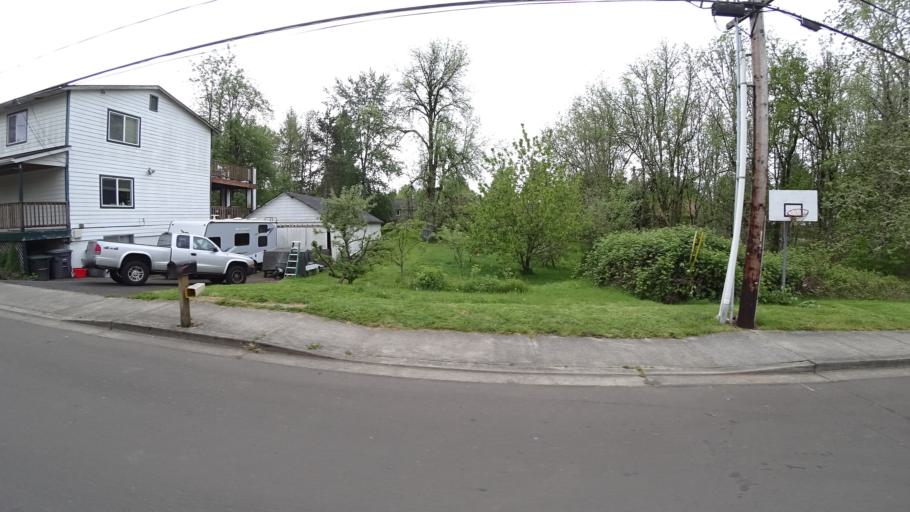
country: US
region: Oregon
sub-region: Washington County
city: Hillsboro
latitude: 45.5445
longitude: -122.9974
